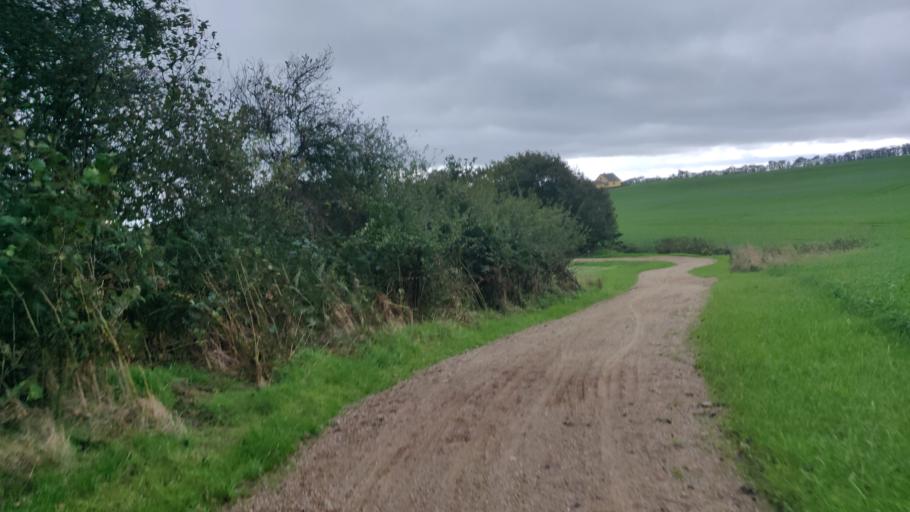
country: DK
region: South Denmark
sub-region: Kolding Kommune
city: Lunderskov
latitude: 55.5414
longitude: 9.3344
